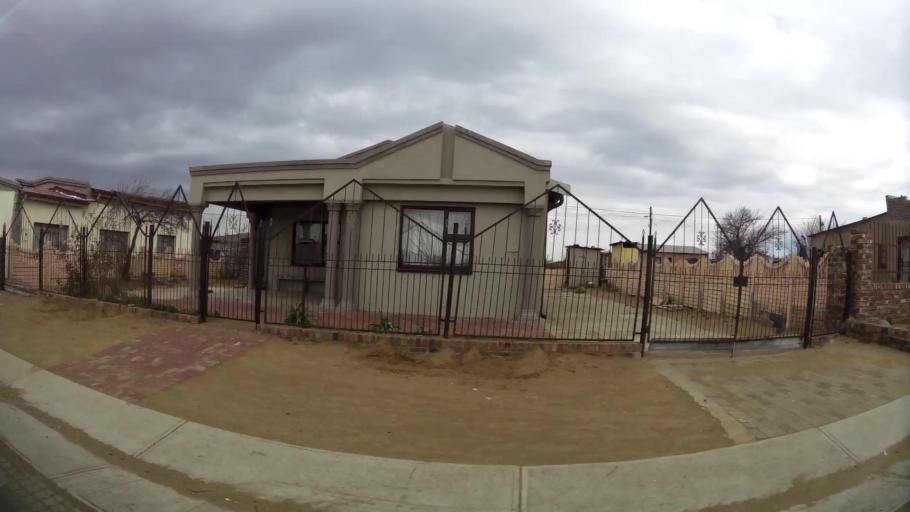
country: ZA
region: Orange Free State
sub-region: Fezile Dabi District Municipality
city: Kroonstad
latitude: -27.6475
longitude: 27.2050
